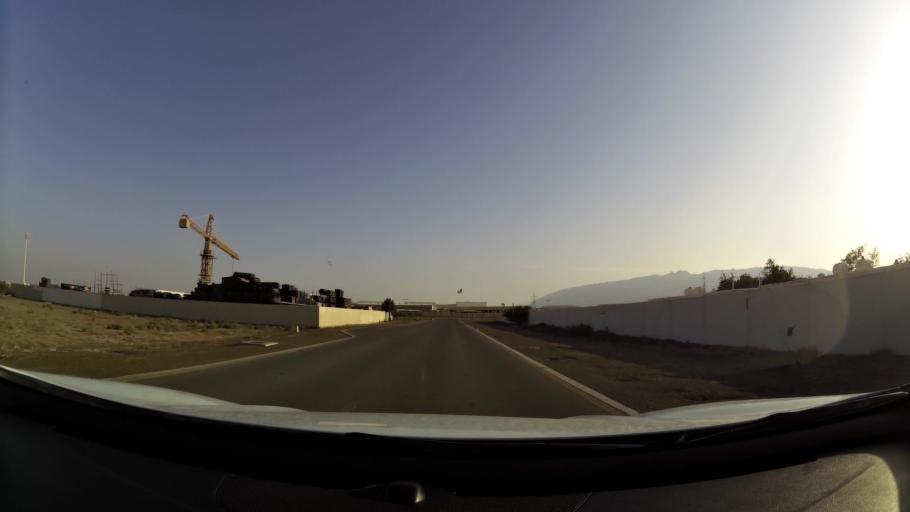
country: AE
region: Abu Dhabi
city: Al Ain
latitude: 24.1383
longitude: 55.8197
